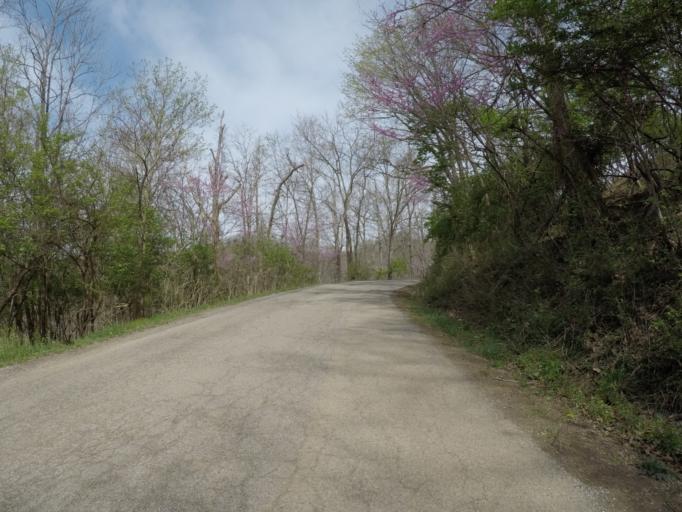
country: US
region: West Virginia
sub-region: Wayne County
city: Lavalette
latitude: 38.3483
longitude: -82.3974
